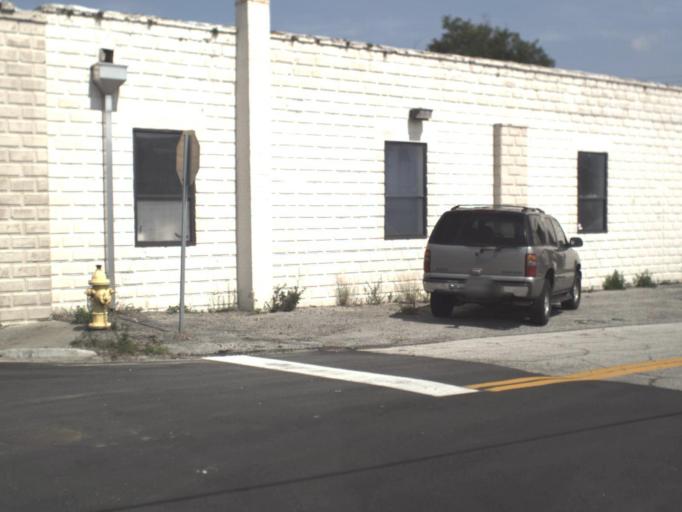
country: US
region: Florida
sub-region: Duval County
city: Jacksonville
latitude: 30.3453
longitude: -81.6337
